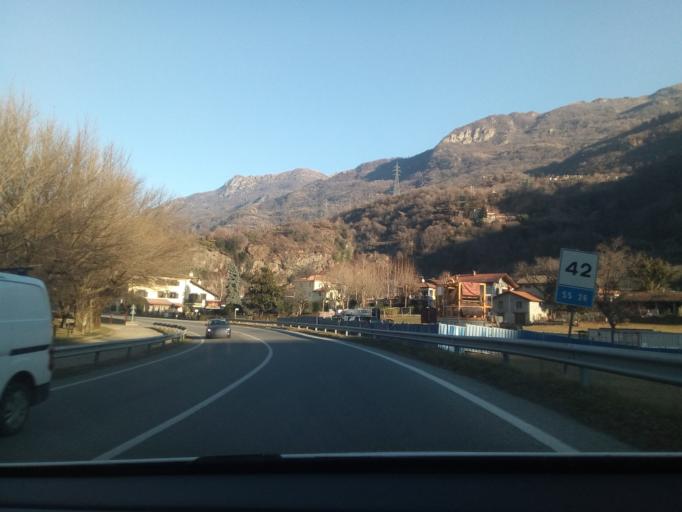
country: IT
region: Piedmont
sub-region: Provincia di Torino
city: Settimo Vittone
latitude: 45.5412
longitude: 7.8378
